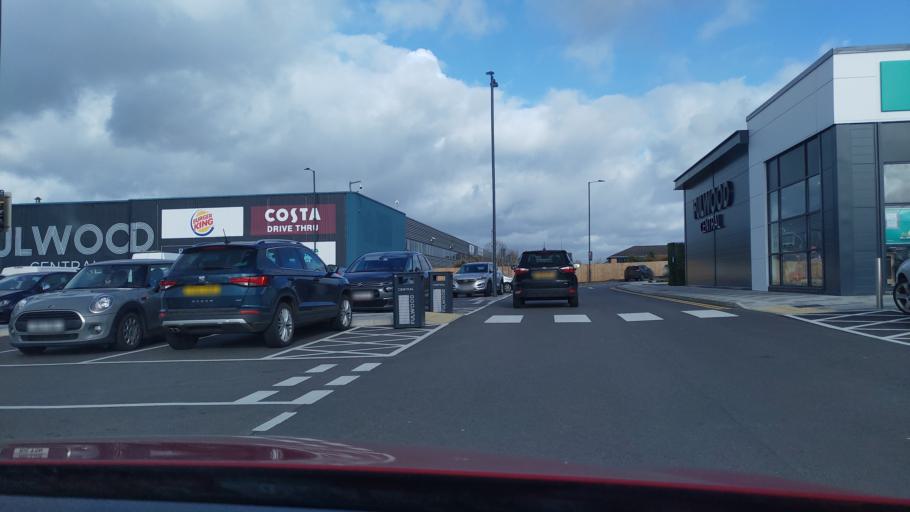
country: GB
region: England
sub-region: Lancashire
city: Goosnargh
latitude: 53.7973
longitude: -2.6944
